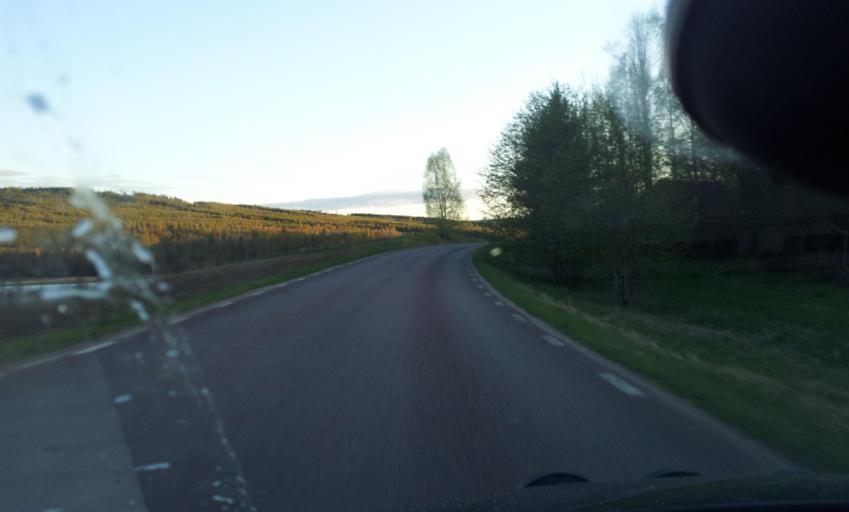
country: SE
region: Gaevleborg
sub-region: Bollnas Kommun
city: Bollnas
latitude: 61.4055
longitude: 16.5373
